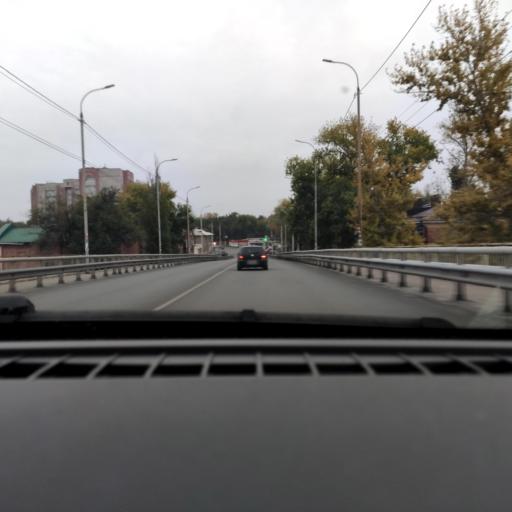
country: RU
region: Voronezj
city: Voronezh
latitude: 51.7259
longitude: 39.2617
